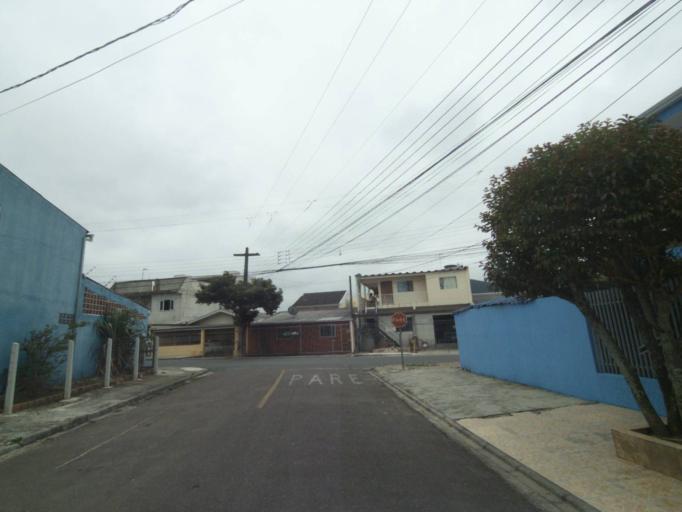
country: BR
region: Parana
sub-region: Sao Jose Dos Pinhais
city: Sao Jose dos Pinhais
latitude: -25.5428
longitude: -49.2560
